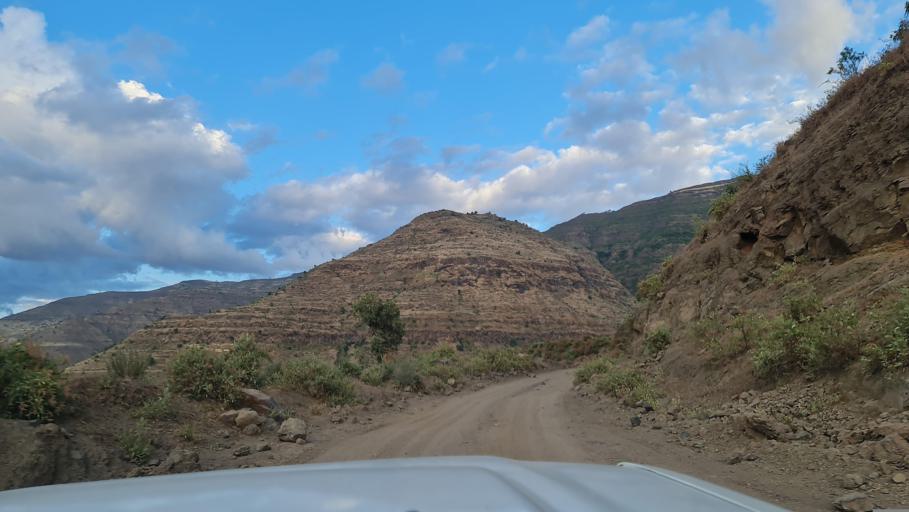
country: ET
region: Amhara
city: Debark'
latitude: 13.0146
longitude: 38.0496
